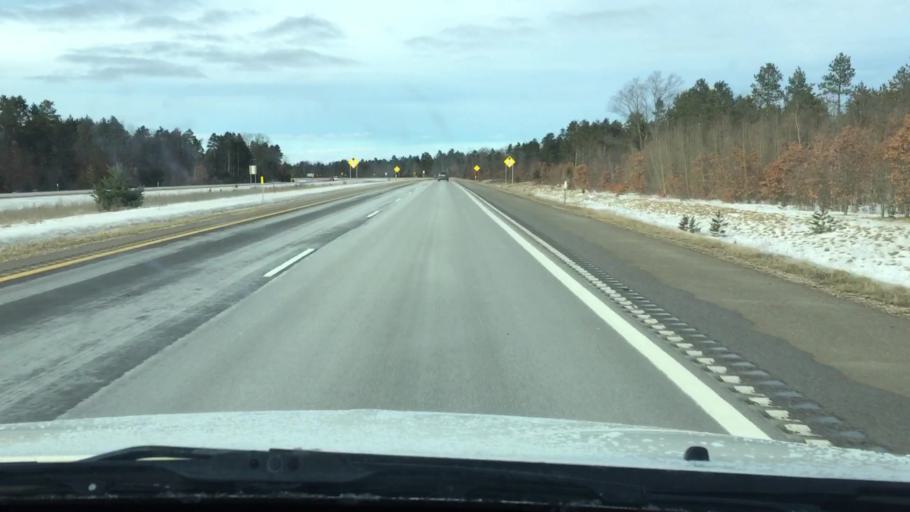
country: US
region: Michigan
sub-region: Wexford County
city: Manton
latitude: 44.4582
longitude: -85.3951
